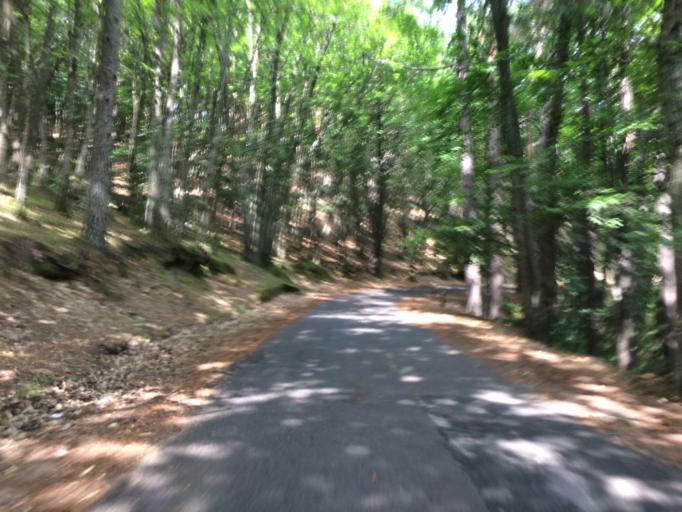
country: IT
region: Liguria
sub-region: Provincia di Imperia
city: Bajardo
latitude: 43.8971
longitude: 7.7299
